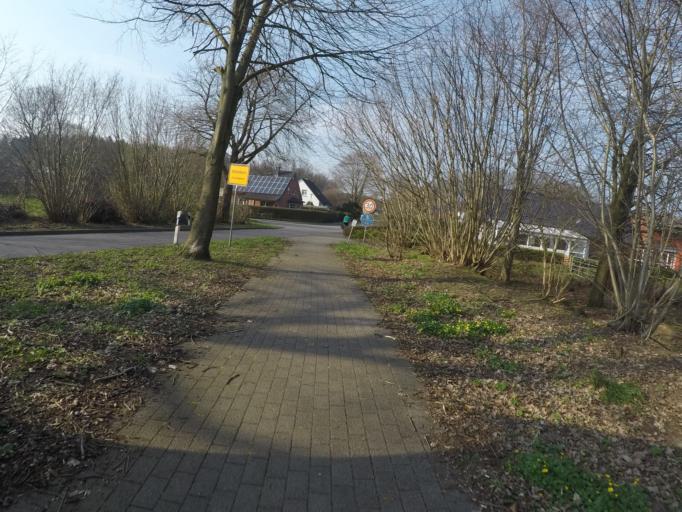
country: DE
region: Schleswig-Holstein
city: Wittenborn
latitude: 53.9200
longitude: 10.2215
